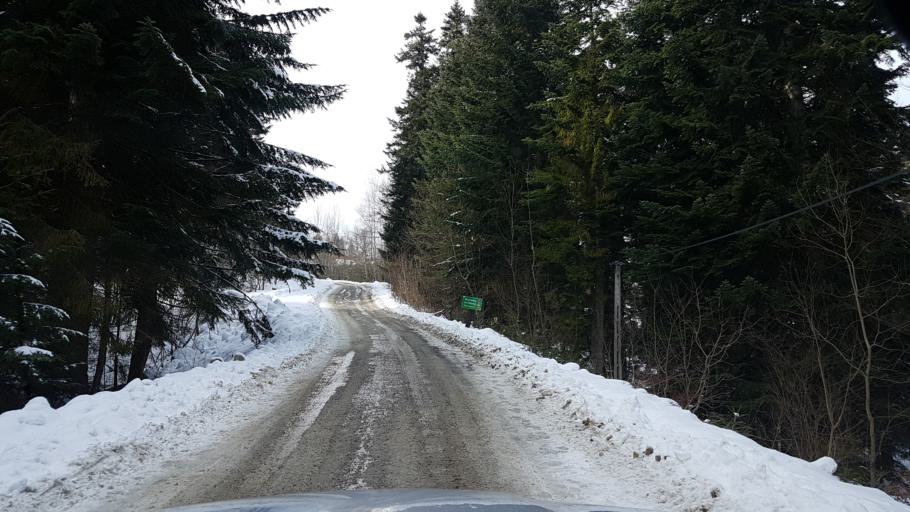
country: PL
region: Lesser Poland Voivodeship
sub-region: Powiat nowosadecki
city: Rytro
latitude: 49.4194
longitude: 20.6282
